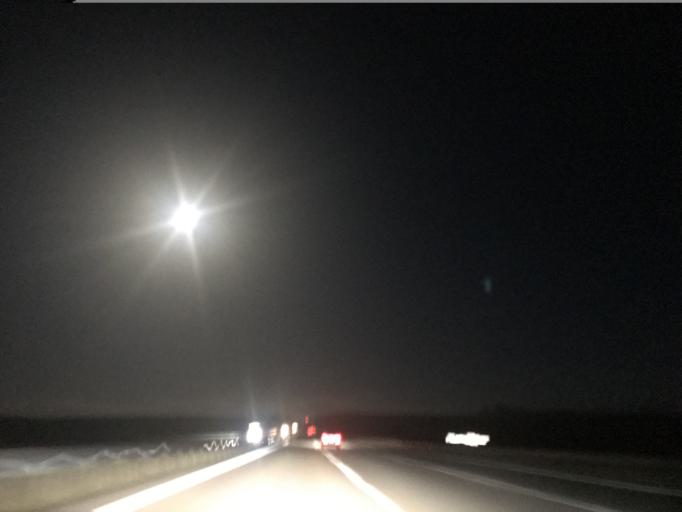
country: TR
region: Nigde
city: Ulukisla
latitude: 37.6396
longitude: 34.3879
